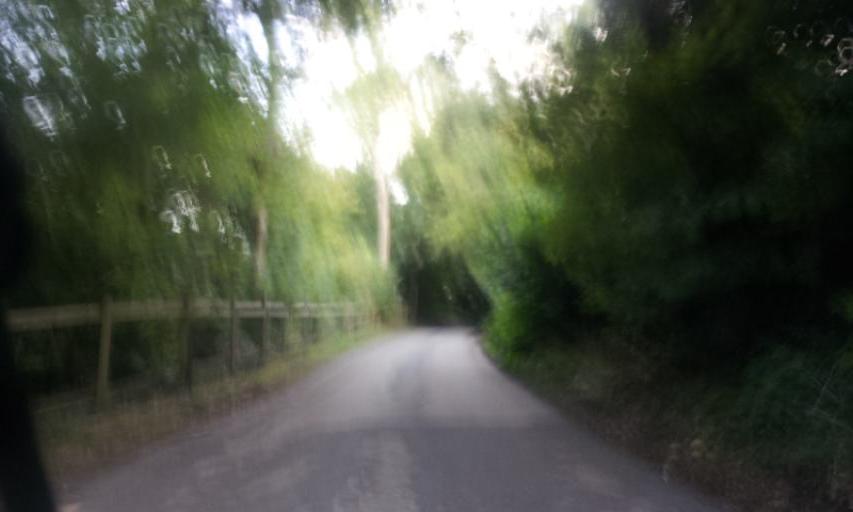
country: GB
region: England
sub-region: Kent
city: Meopham
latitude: 51.3769
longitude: 0.4008
